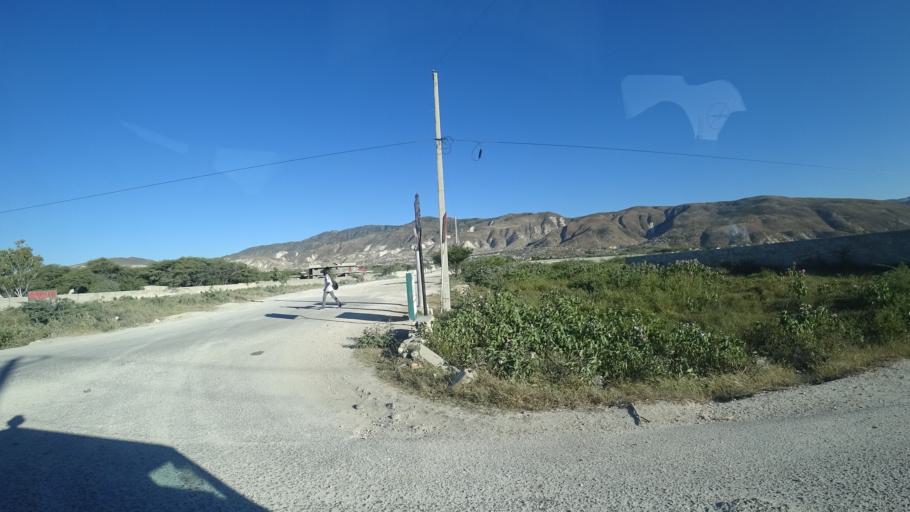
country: HT
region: Ouest
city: Croix des Bouquets
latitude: 18.6489
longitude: -72.2313
